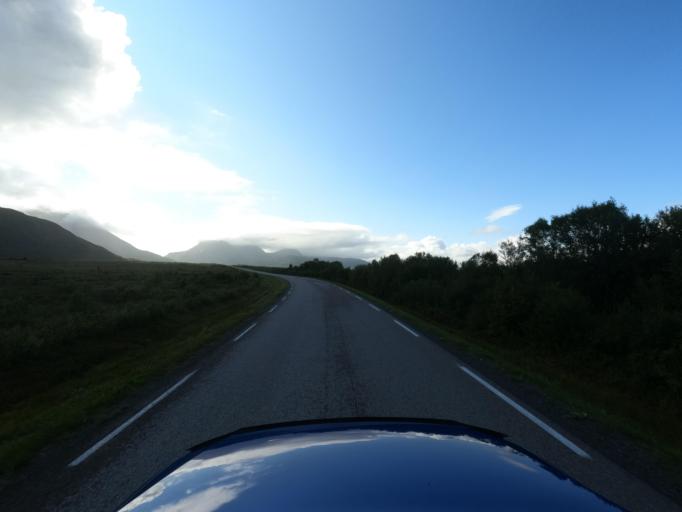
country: NO
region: Nordland
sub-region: Vagan
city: Kabelvag
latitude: 68.3080
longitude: 14.1997
